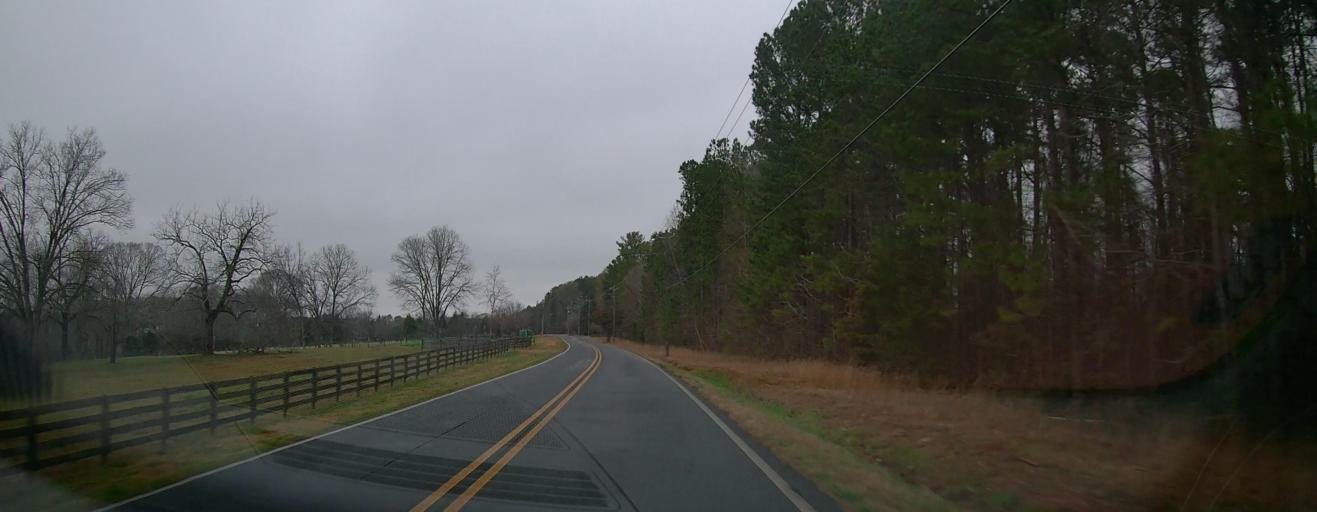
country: US
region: Georgia
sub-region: Pike County
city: Zebulon
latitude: 33.1405
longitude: -84.3459
